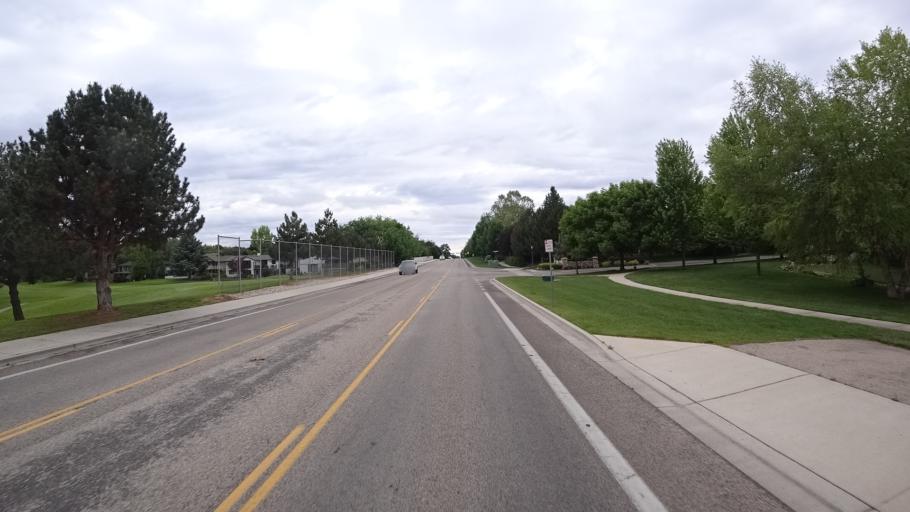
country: US
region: Idaho
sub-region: Ada County
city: Eagle
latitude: 43.7065
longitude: -116.3397
